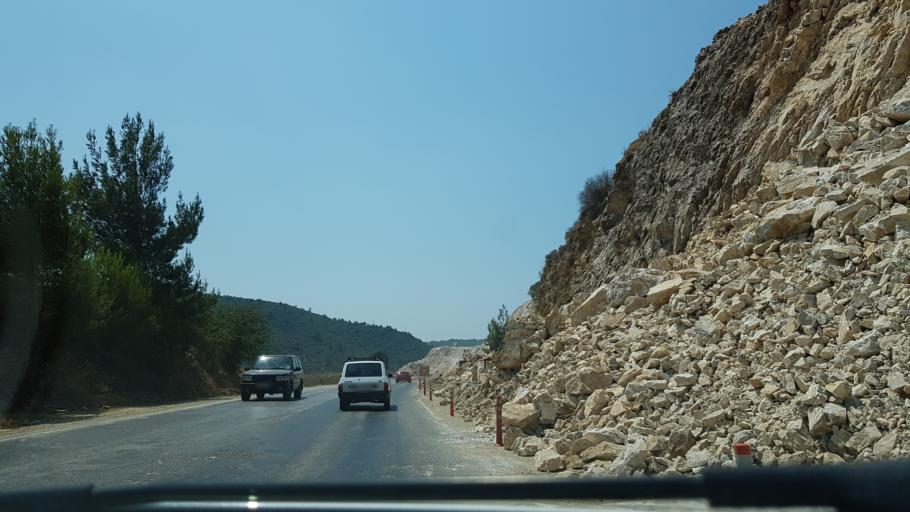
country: TR
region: Aydin
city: Ortaklar
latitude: 37.8951
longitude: 27.4732
